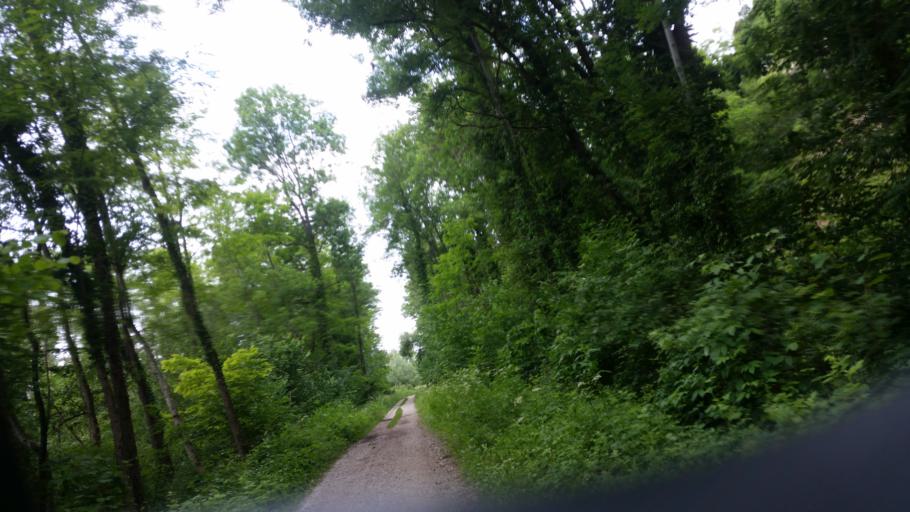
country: CH
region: Fribourg
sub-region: Broye District
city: Estavayer-le-Lac
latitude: 46.8334
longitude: 6.8106
